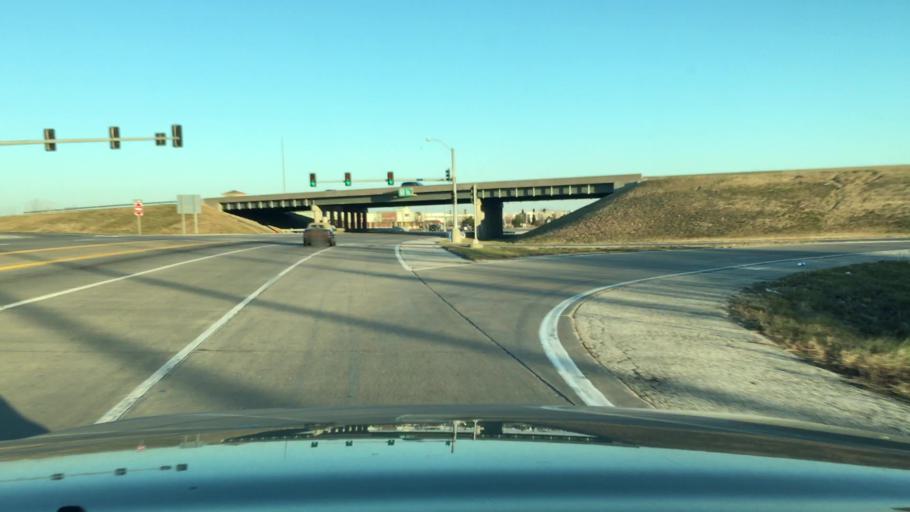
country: US
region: Missouri
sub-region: Saint Charles County
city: Saint Charles
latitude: 38.8229
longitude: -90.5175
